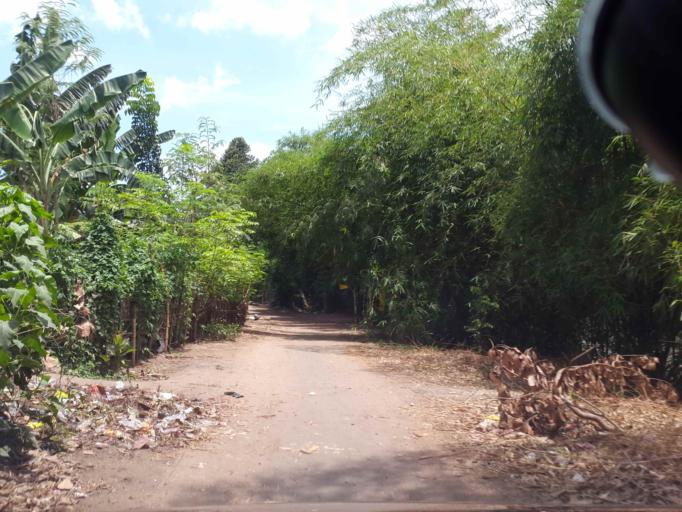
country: ID
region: West Nusa Tenggara
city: Jelateng Timur
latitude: -8.6954
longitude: 116.0931
